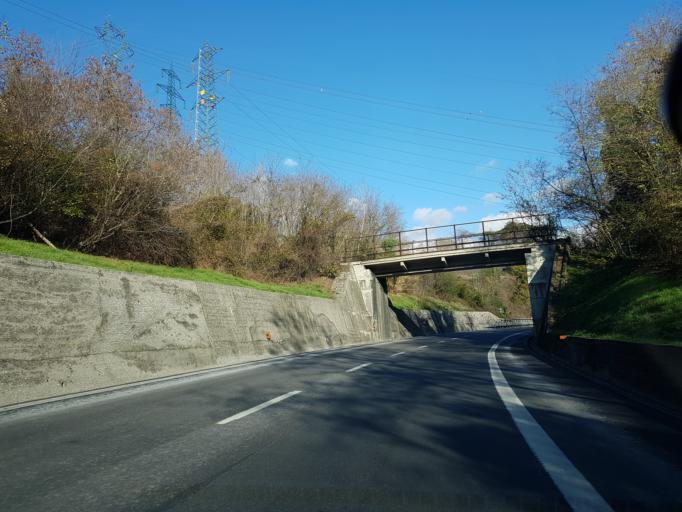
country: IT
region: Liguria
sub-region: Provincia di Genova
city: Manesseno
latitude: 44.4782
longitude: 8.9114
